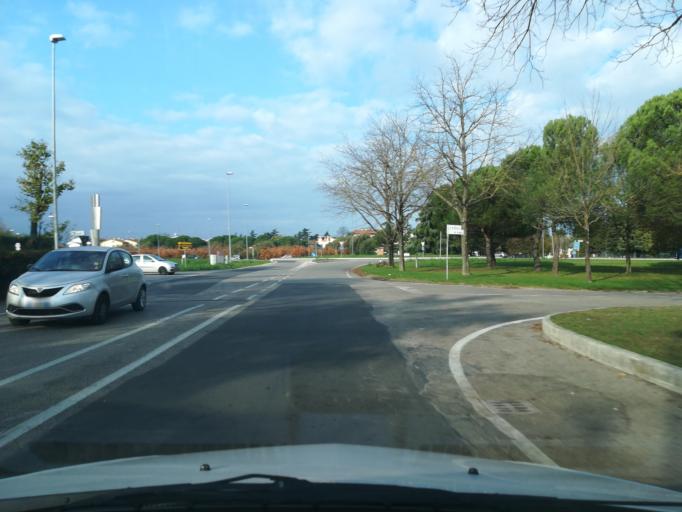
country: IT
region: Emilia-Romagna
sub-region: Provincia di Bologna
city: Imola
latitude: 44.3678
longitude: 11.7048
